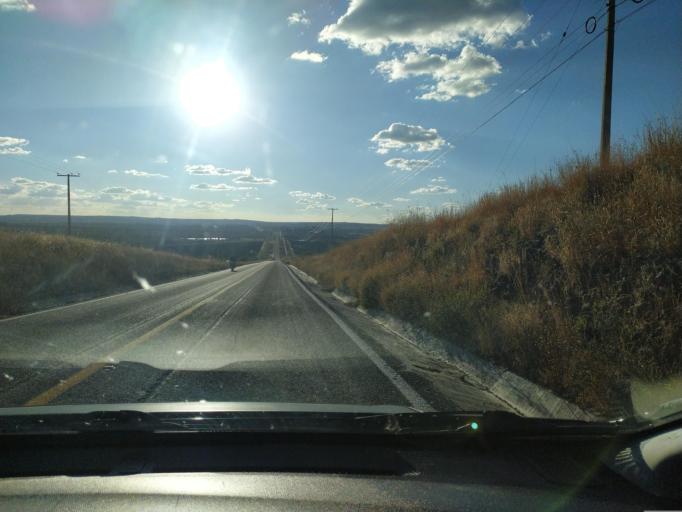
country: MX
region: Guanajuato
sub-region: Purisima del Rincon
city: Monte Grande
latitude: 21.0282
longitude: -101.9284
